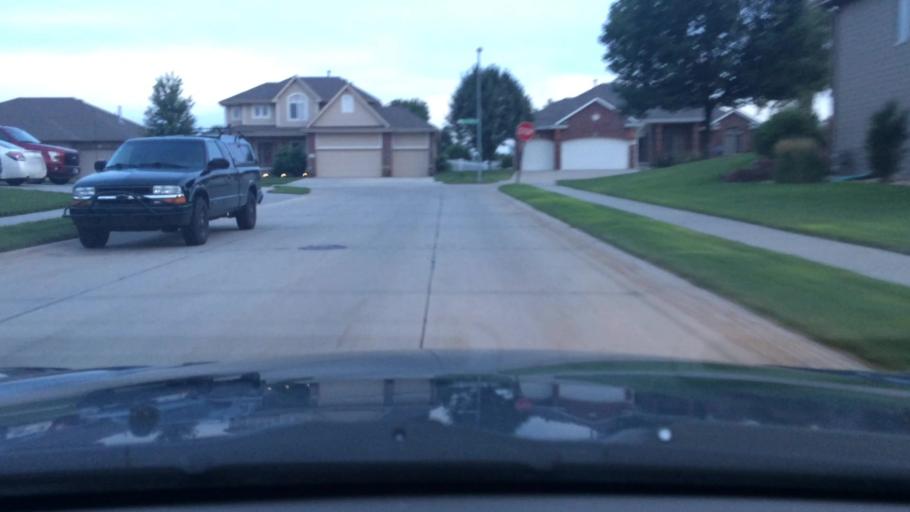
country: US
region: Nebraska
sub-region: Douglas County
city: Ralston
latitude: 41.1843
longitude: -96.0578
